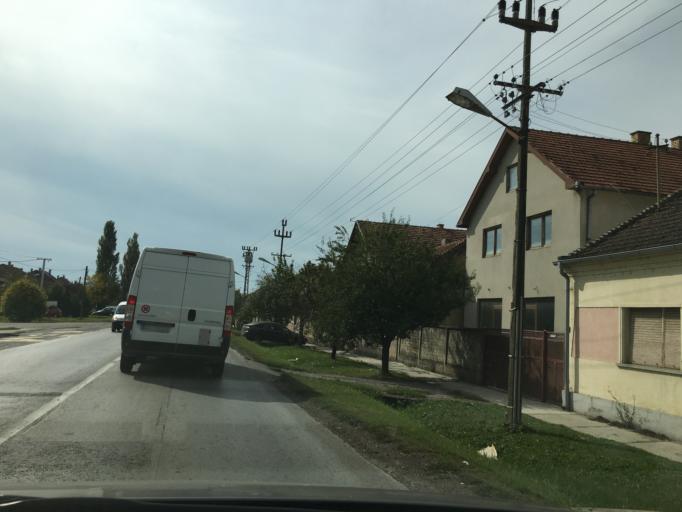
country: RS
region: Autonomna Pokrajina Vojvodina
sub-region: Juznobacki Okrug
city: Temerin
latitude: 45.3677
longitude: 19.8695
